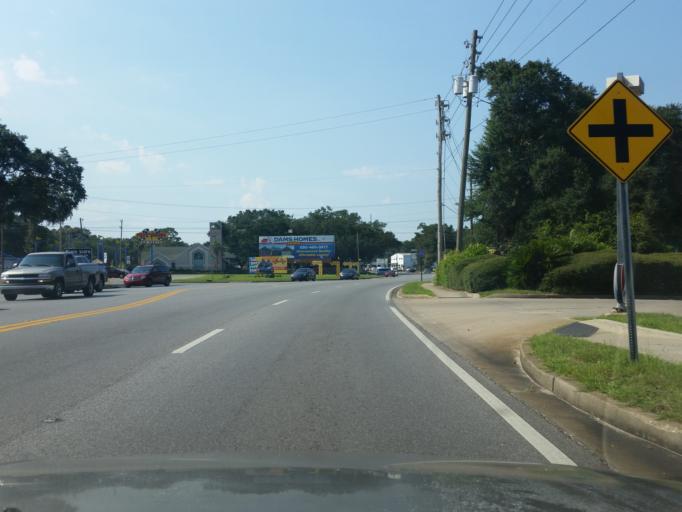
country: US
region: Florida
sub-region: Escambia County
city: Brent
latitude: 30.4643
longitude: -87.2529
